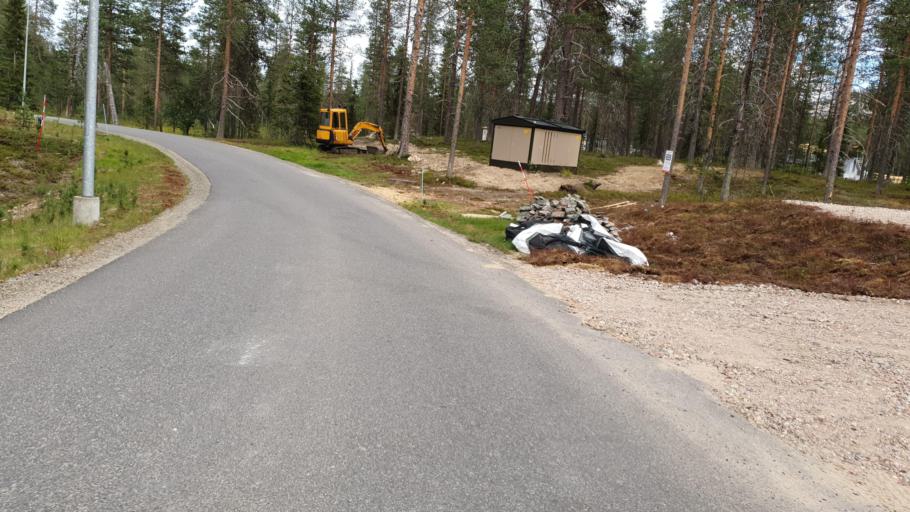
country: FI
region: Lapland
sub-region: Tunturi-Lappi
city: Kolari
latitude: 67.5979
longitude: 24.1339
